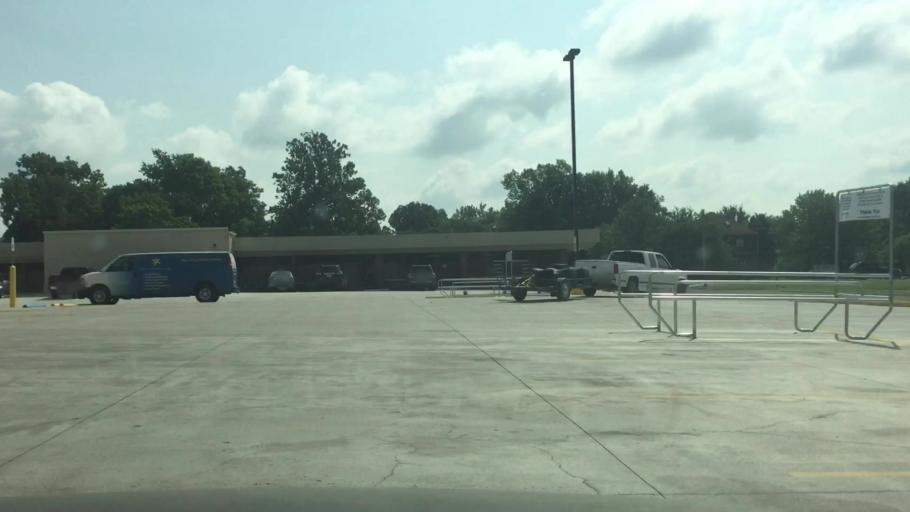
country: US
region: Kansas
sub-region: Allen County
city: Iola
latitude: 37.9212
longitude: -95.3951
